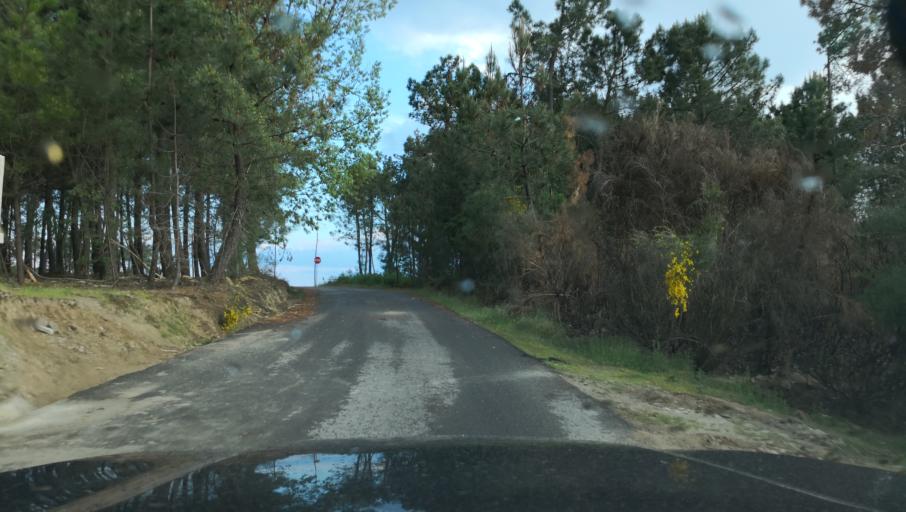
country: PT
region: Vila Real
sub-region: Vila Real
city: Vila Real
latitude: 41.3181
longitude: -7.6868
